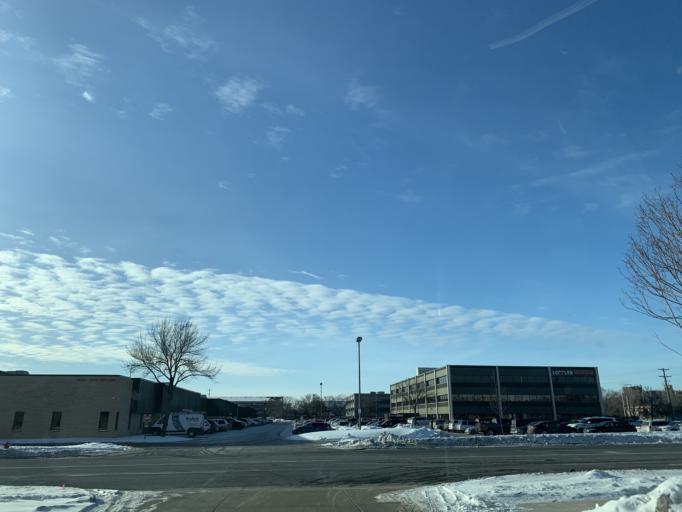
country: US
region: Minnesota
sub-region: Hennepin County
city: Richfield
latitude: 44.8610
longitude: -93.2577
